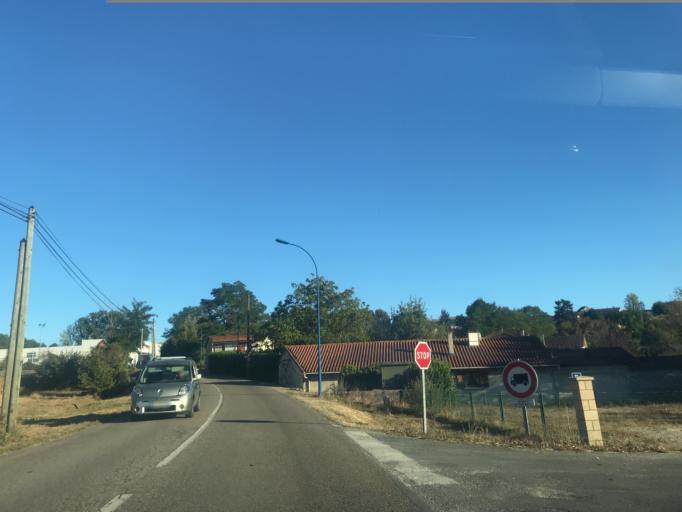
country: FR
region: Poitou-Charentes
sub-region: Departement de la Charente-Maritime
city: Saint-Aigulin
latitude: 45.1571
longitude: 0.0047
